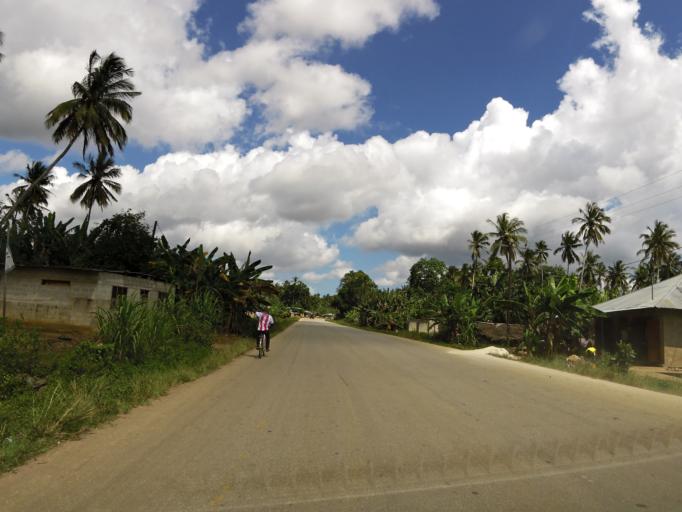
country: TZ
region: Zanzibar Central/South
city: Koani
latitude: -6.1337
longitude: 39.2957
